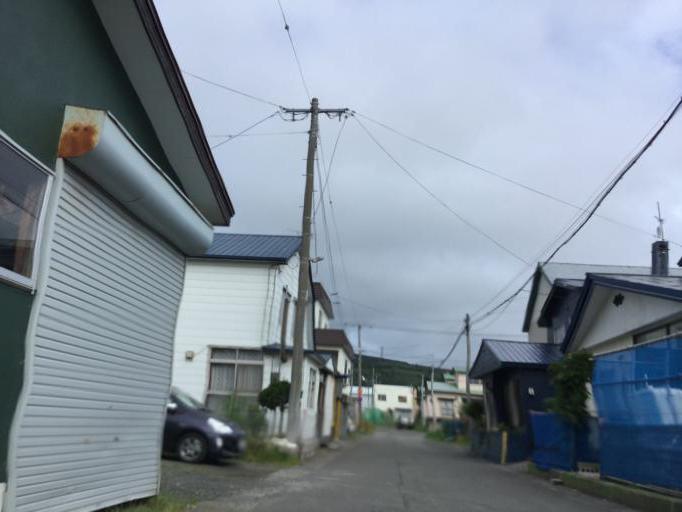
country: JP
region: Hokkaido
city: Wakkanai
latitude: 45.4016
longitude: 141.6822
